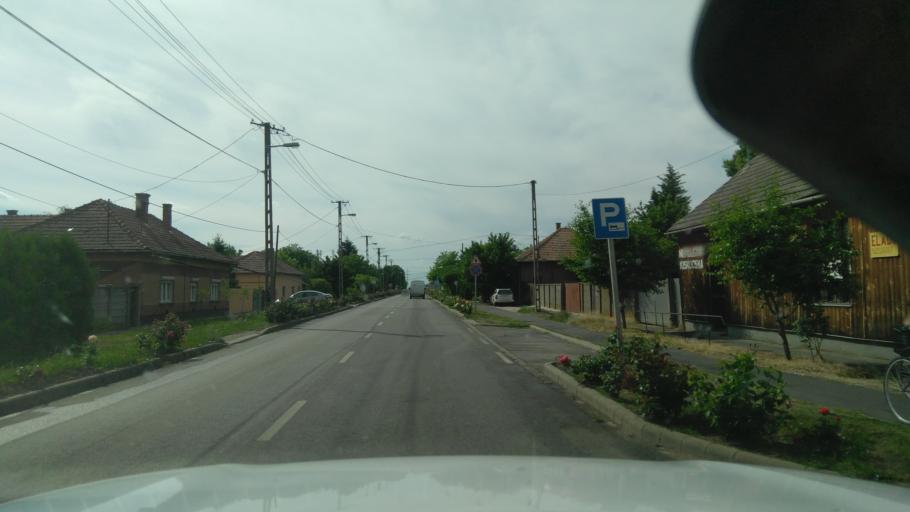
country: HU
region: Bekes
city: Medgyesegyhaza
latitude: 46.5024
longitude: 21.0189
